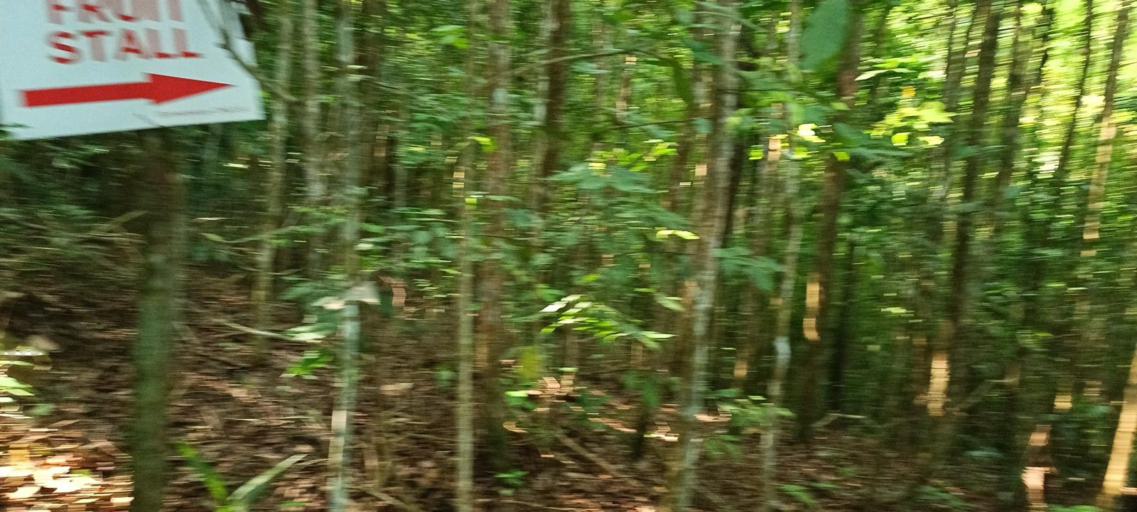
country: MY
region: Penang
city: Bukit Mertajam
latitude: 5.3663
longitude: 100.4973
